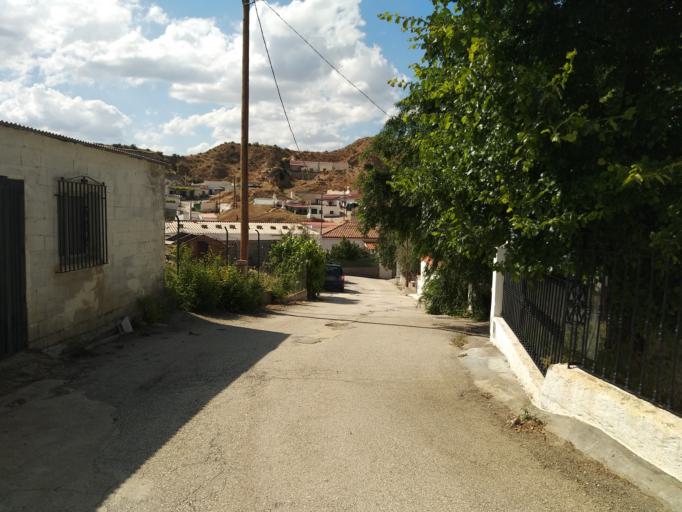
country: ES
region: Andalusia
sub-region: Provincia de Granada
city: Marchal
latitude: 37.3020
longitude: -3.2109
